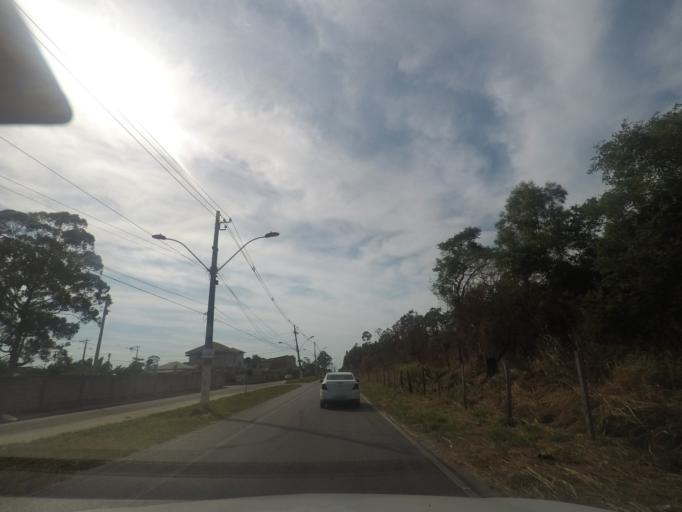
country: BR
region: Rio de Janeiro
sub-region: Marica
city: Marica
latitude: -22.9409
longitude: -42.8947
